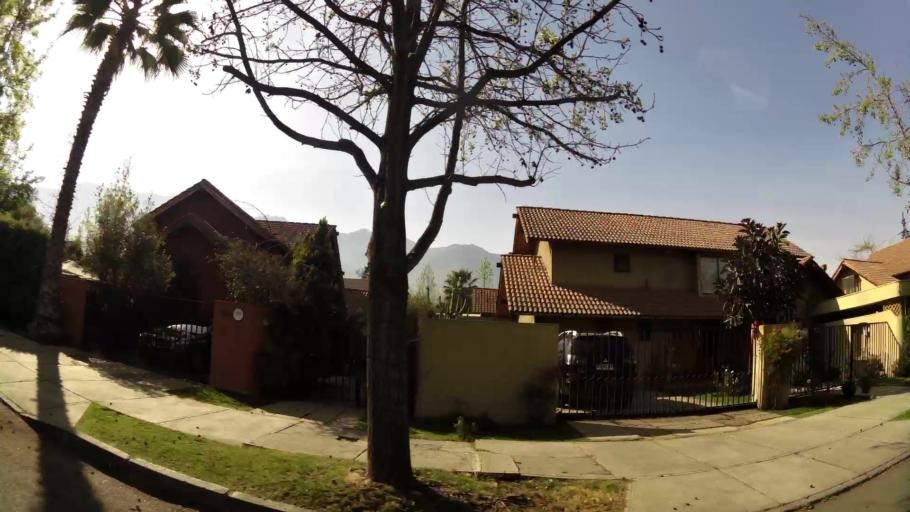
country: CL
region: Santiago Metropolitan
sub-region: Provincia de Santiago
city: Villa Presidente Frei, Nunoa, Santiago, Chile
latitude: -33.4877
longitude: -70.5426
